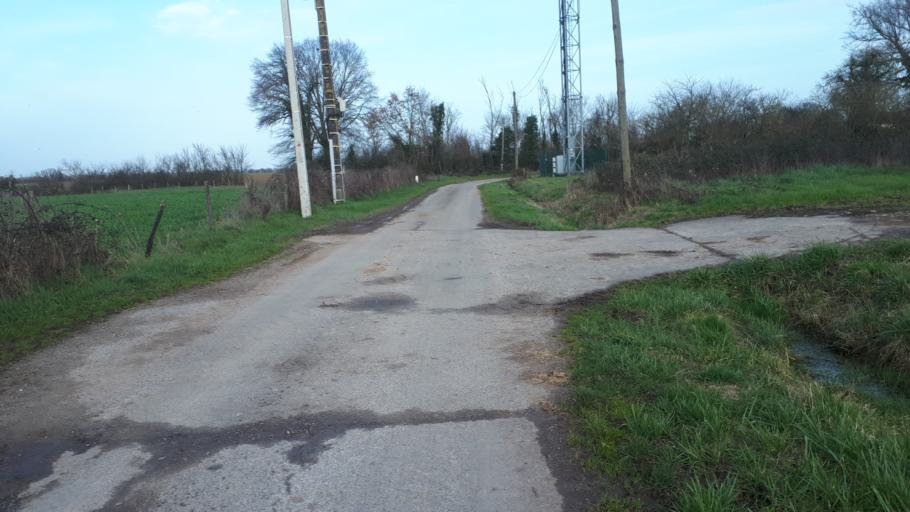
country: FR
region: Poitou-Charentes
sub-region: Departement de la Vienne
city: Archigny
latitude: 46.6202
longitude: 0.7534
